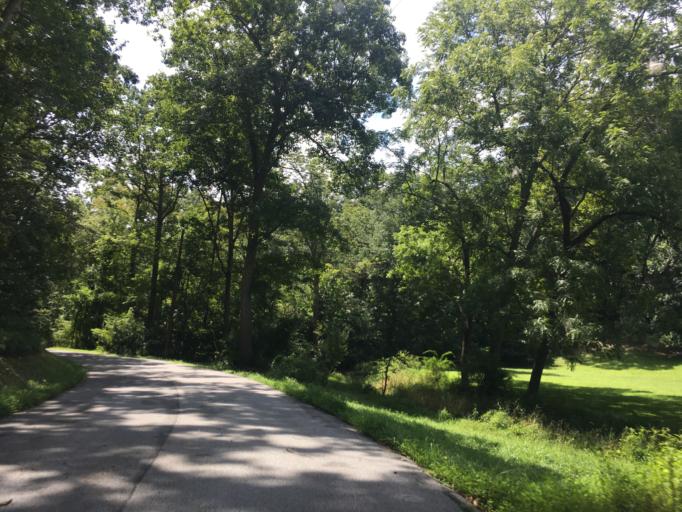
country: US
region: Pennsylvania
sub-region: York County
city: New Freedom
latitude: 39.6913
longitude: -76.6546
